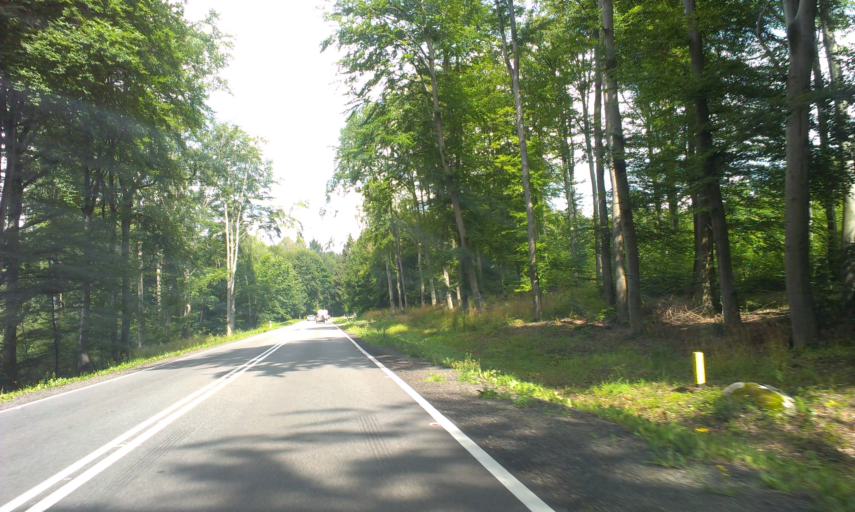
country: PL
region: West Pomeranian Voivodeship
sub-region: Powiat koszalinski
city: Bobolice
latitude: 53.9260
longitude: 16.5999
